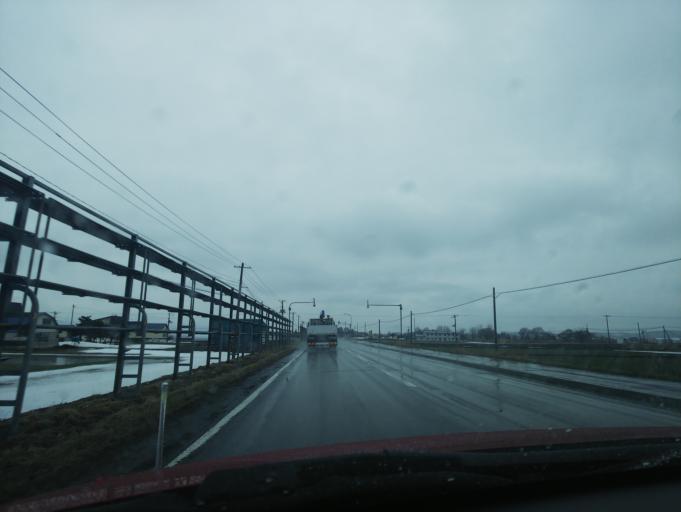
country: JP
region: Hokkaido
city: Nayoro
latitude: 44.2043
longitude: 142.3949
